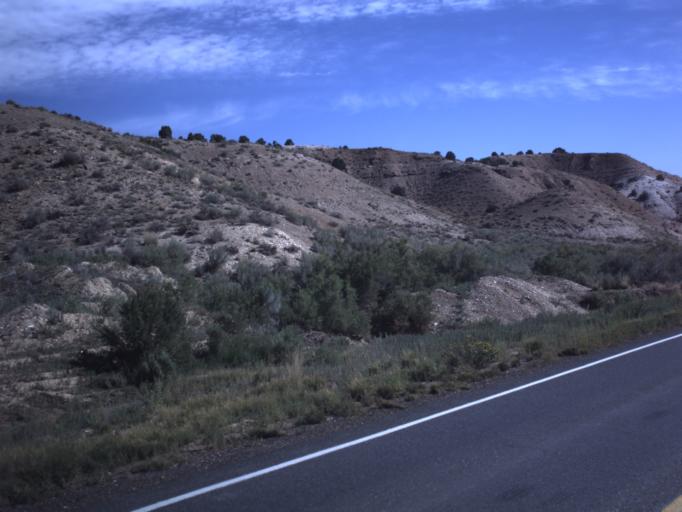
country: US
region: Utah
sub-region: Duchesne County
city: Duchesne
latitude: 40.1264
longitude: -110.4412
